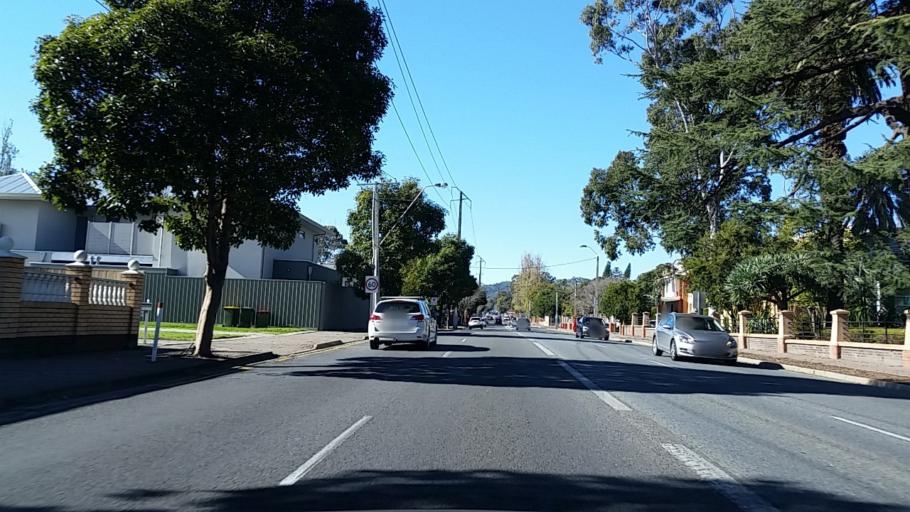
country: AU
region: South Australia
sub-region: Norwood Payneham St Peters
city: Trinity Gardens
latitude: -34.9272
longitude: 138.6373
